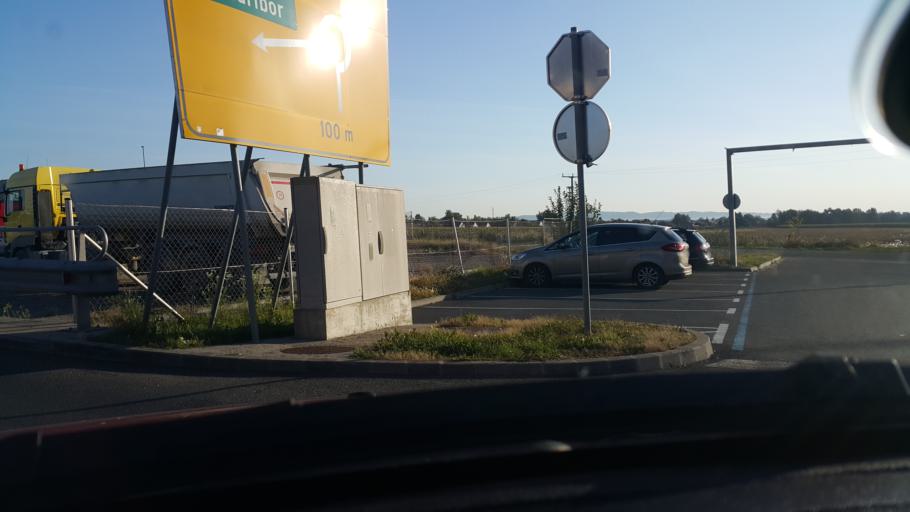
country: SI
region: Hoce-Slivnica
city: Hotinja Vas
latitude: 46.4502
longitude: 15.6537
